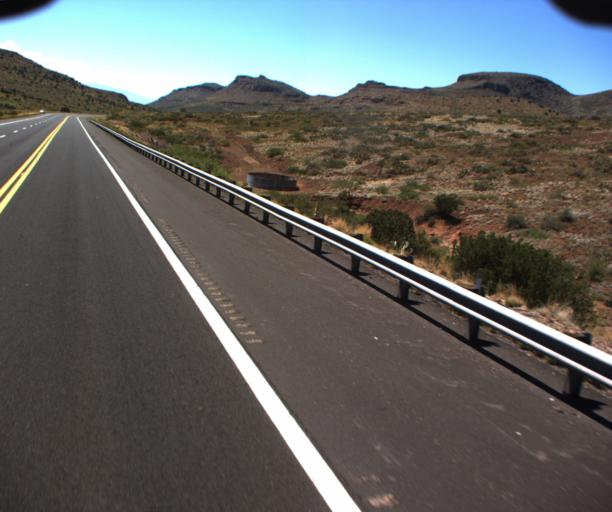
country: US
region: Arizona
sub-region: Greenlee County
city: Clifton
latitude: 32.8518
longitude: -109.3097
